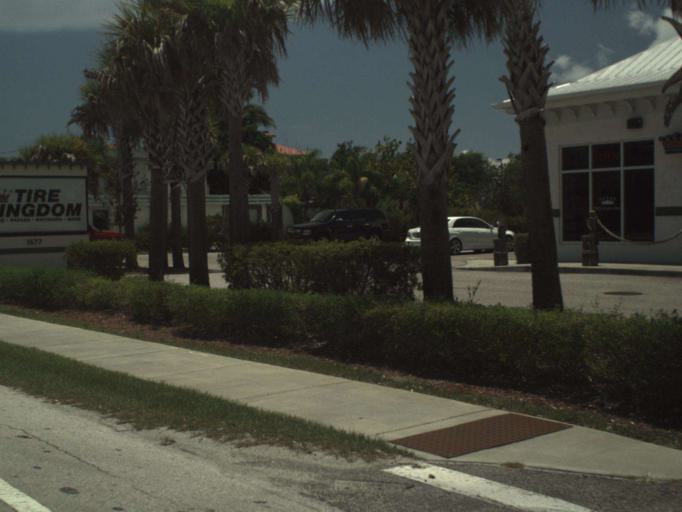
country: US
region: Florida
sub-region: Indian River County
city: Sebastian
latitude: 27.8262
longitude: -80.4764
